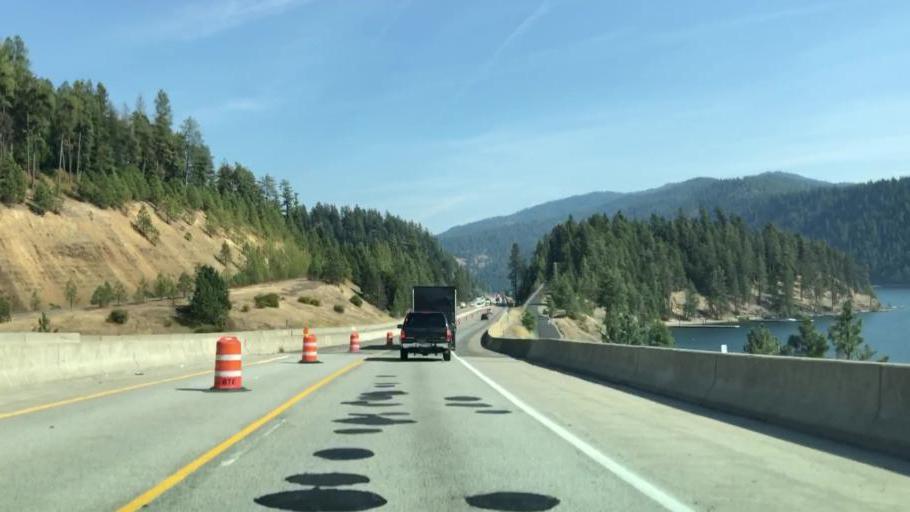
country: US
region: Idaho
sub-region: Kootenai County
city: Coeur d'Alene
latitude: 47.6301
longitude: -116.6864
